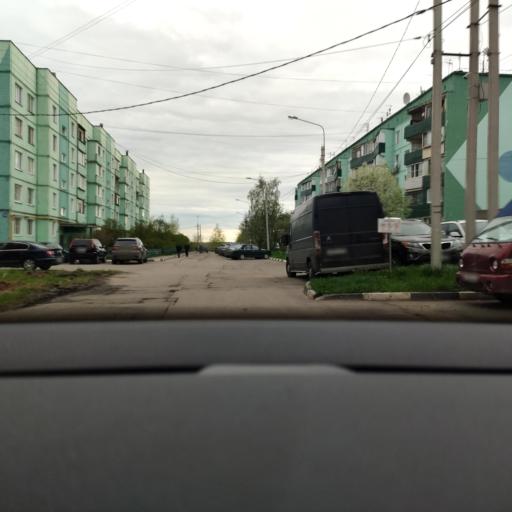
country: RU
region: Moskovskaya
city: Novopodrezkovo
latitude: 55.9919
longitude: 37.3395
